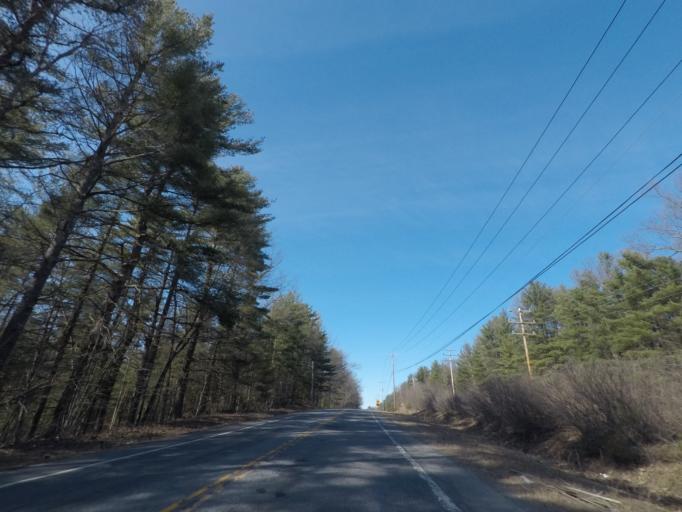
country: US
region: New York
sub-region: Saratoga County
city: Milton
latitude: 43.0535
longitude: -73.8506
